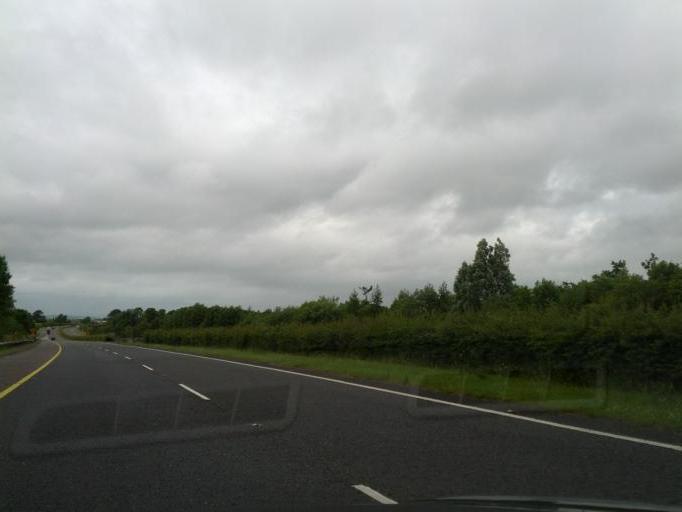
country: IE
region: Munster
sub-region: An Clar
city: Newmarket on Fergus
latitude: 52.7515
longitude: -8.9020
